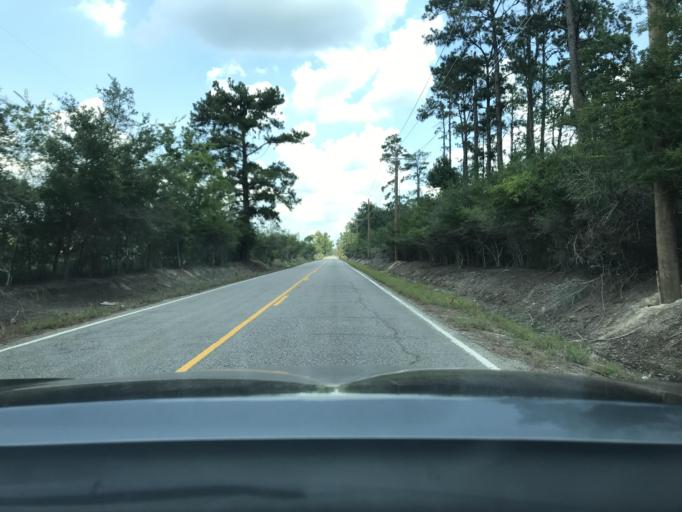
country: US
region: Louisiana
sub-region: Calcasieu Parish
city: Moss Bluff
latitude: 30.3300
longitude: -93.1674
